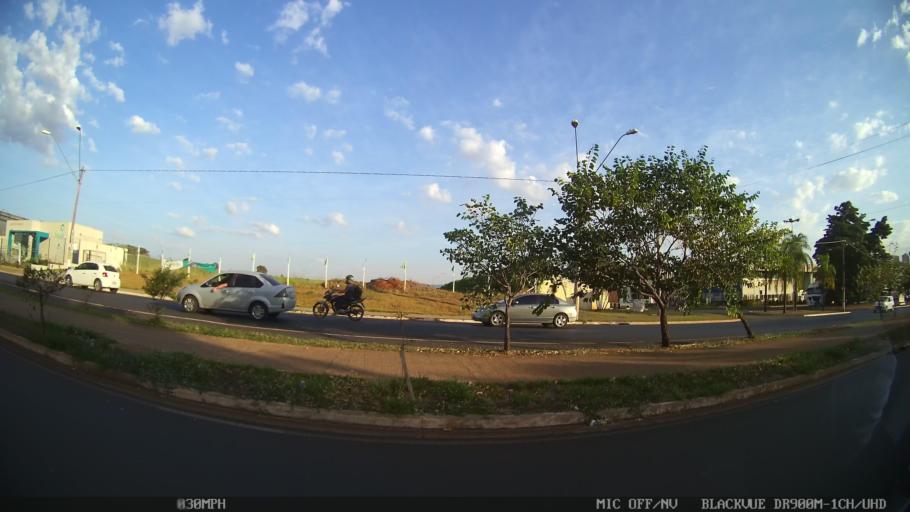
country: BR
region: Sao Paulo
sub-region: Ribeirao Preto
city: Ribeirao Preto
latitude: -21.1934
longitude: -47.7530
